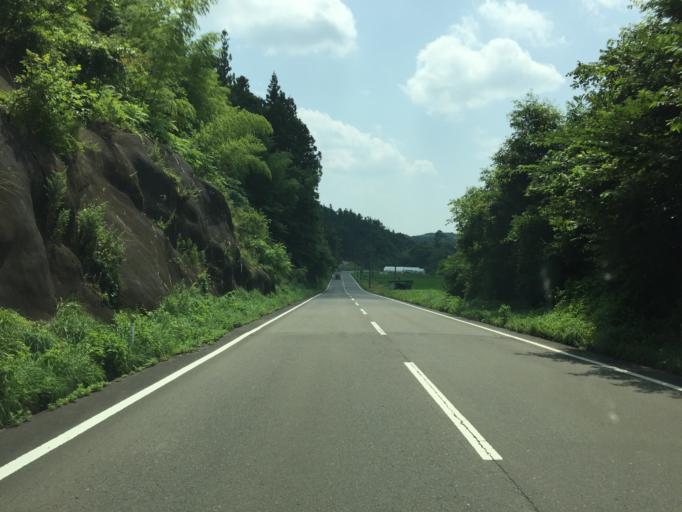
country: JP
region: Fukushima
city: Ishikawa
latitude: 37.2309
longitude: 140.5599
